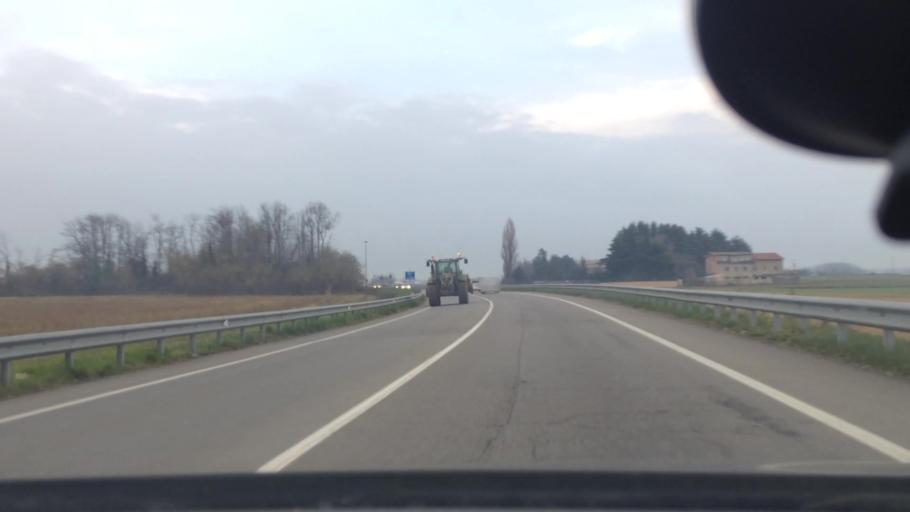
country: IT
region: Lombardy
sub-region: Provincia di Monza e Brianza
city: Ceriano Laghetto
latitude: 45.6258
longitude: 9.0600
